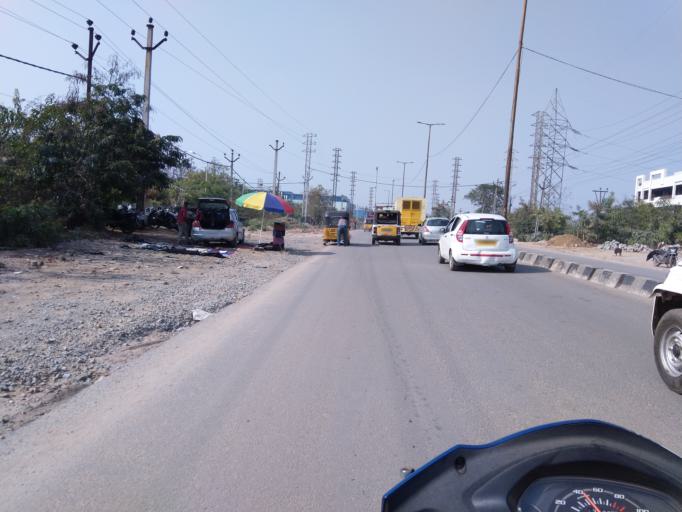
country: IN
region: Telangana
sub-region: Rangareddi
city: Quthbullapur
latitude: 17.5306
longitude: 78.4369
